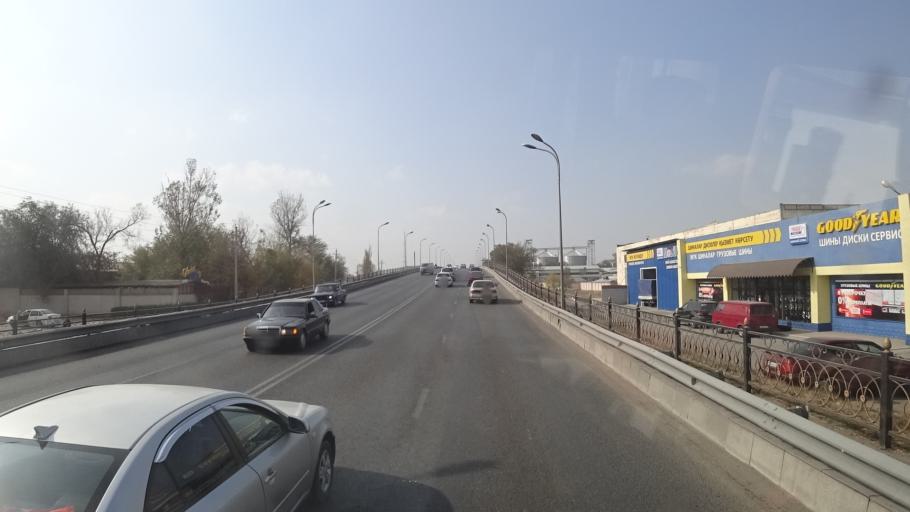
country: KZ
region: Zhambyl
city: Taraz
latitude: 42.9229
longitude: 71.4121
